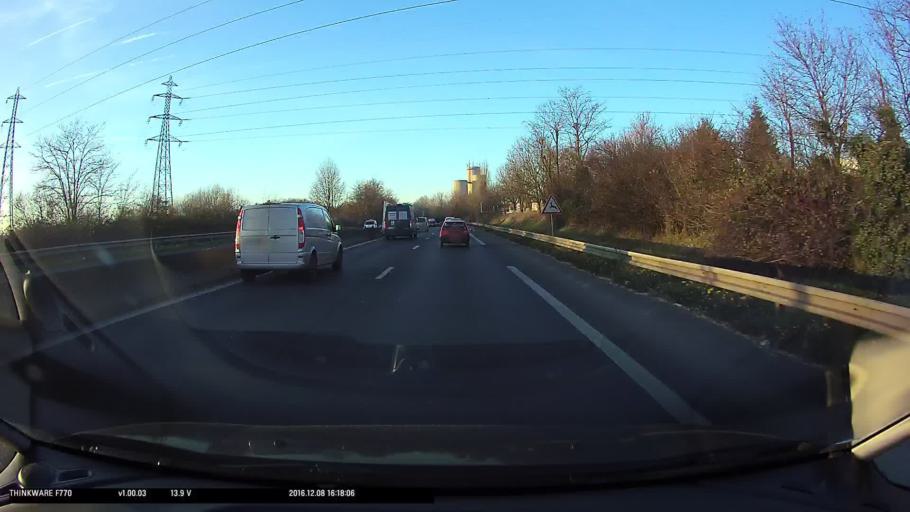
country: FR
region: Ile-de-France
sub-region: Departement du Val-d'Oise
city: Cergy-Pontoise
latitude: 49.0485
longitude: 2.0707
